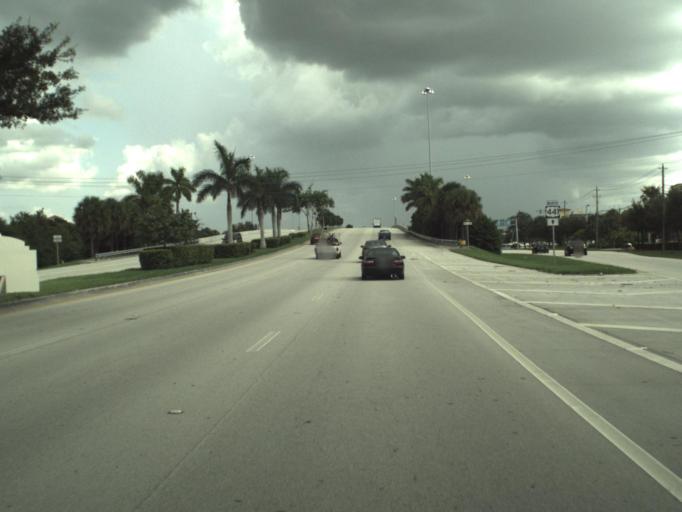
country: US
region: Florida
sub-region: Broward County
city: Margate
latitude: 26.2709
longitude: -80.2016
